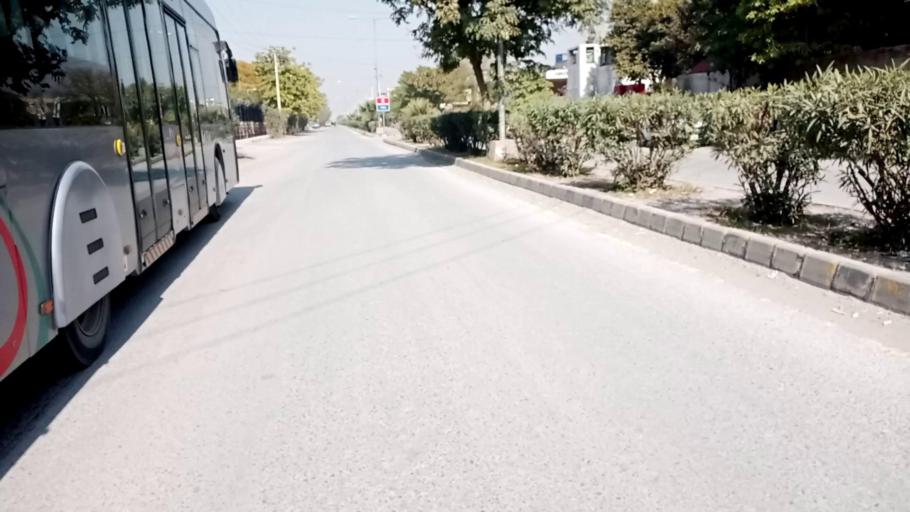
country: PK
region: Khyber Pakhtunkhwa
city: Peshawar
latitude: 33.9575
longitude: 71.4177
